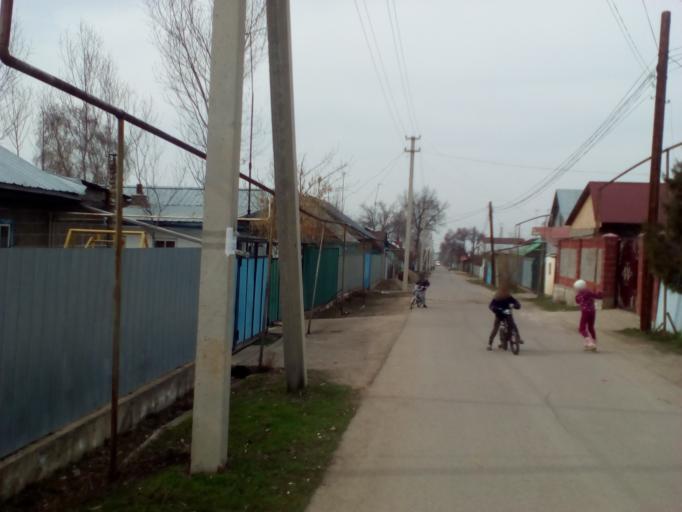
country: KZ
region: Almaty Oblysy
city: Burunday
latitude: 43.1580
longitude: 76.4098
